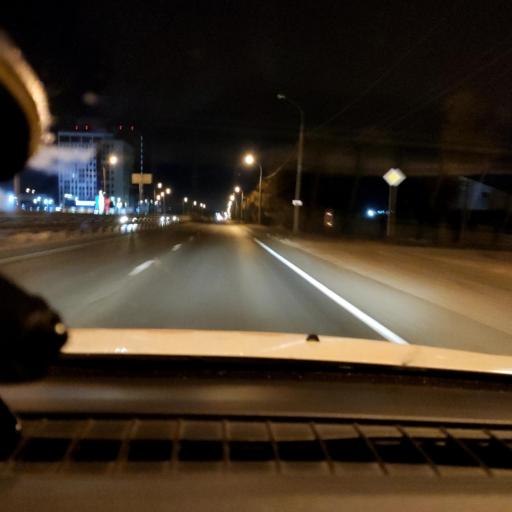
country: RU
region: Samara
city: Samara
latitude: 53.1147
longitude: 50.1664
